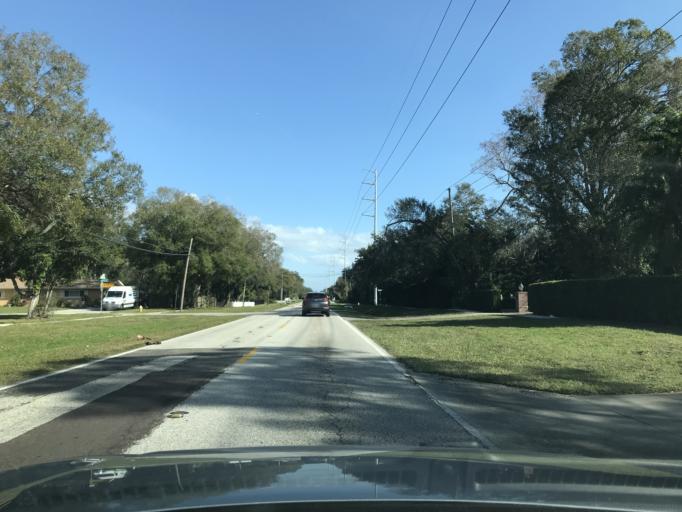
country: US
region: Florida
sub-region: Pinellas County
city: South Highpoint
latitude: 27.9386
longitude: -82.7529
